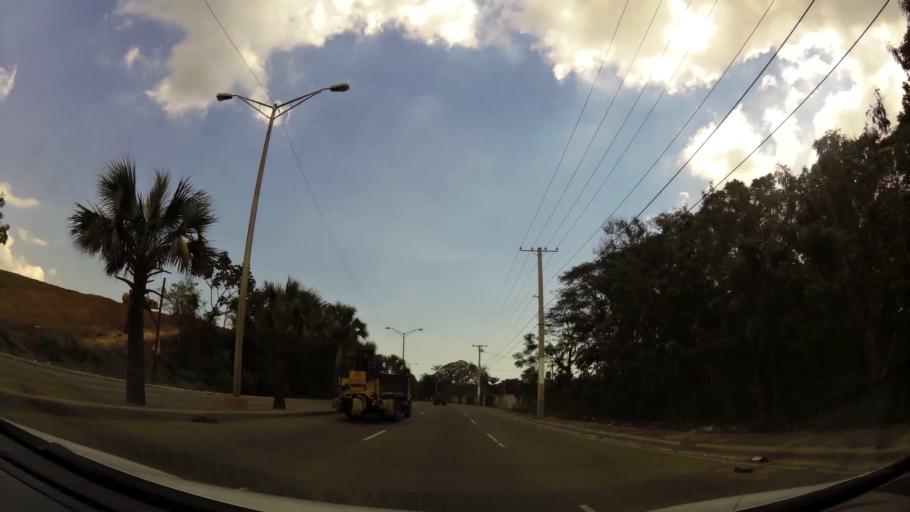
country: DO
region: Nacional
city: La Agustina
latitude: 18.5312
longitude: -69.9549
